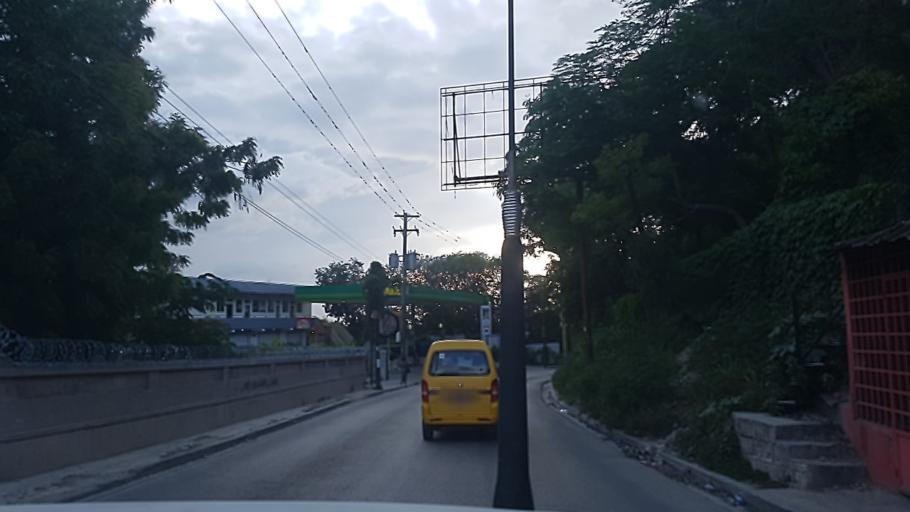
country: HT
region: Ouest
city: Petionville
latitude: 18.5252
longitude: -72.2966
